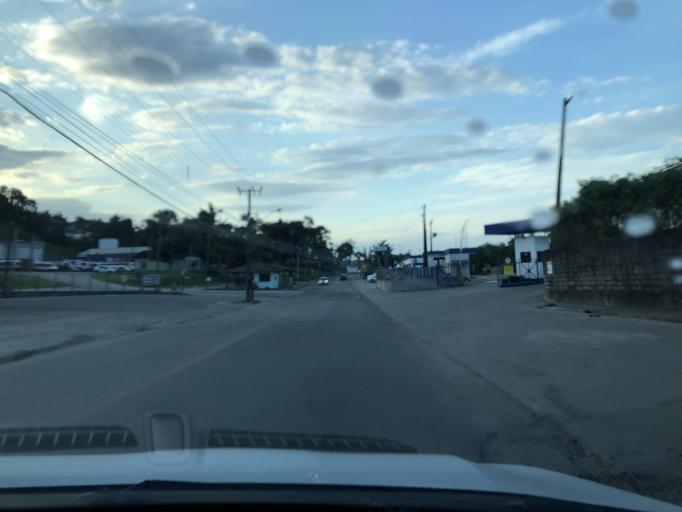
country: BR
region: Santa Catarina
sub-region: Sao Francisco Do Sul
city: Sao Francisco do Sul
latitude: -26.2577
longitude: -48.6233
